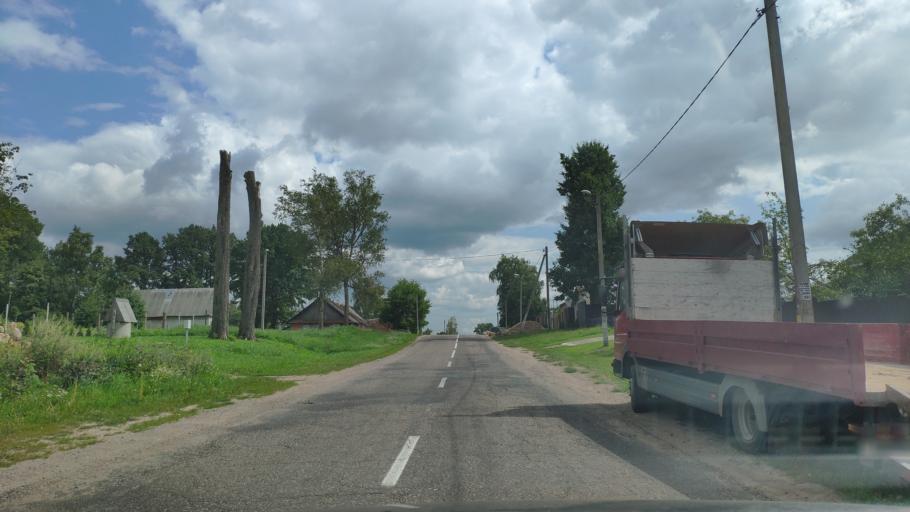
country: BY
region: Minsk
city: Khatsyezhyna
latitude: 53.8879
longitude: 27.2654
